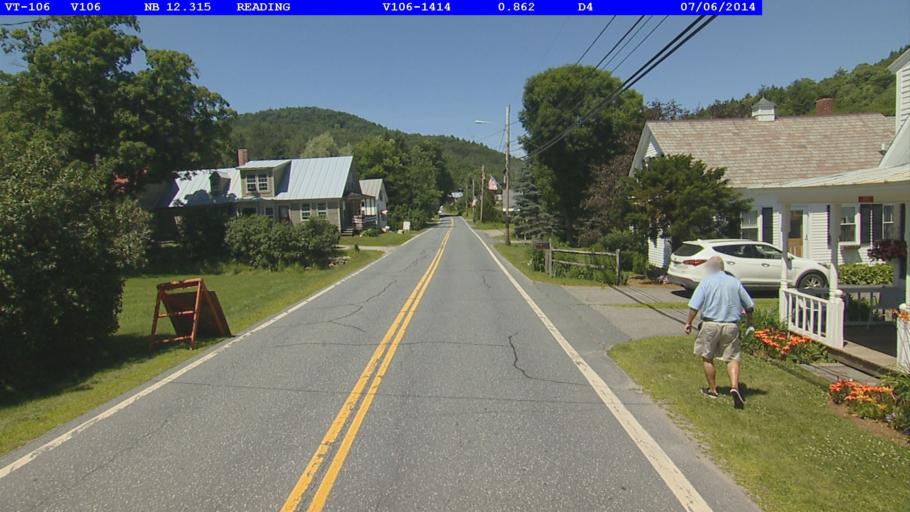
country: US
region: Vermont
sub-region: Windsor County
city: Windsor
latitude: 43.4566
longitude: -72.5371
